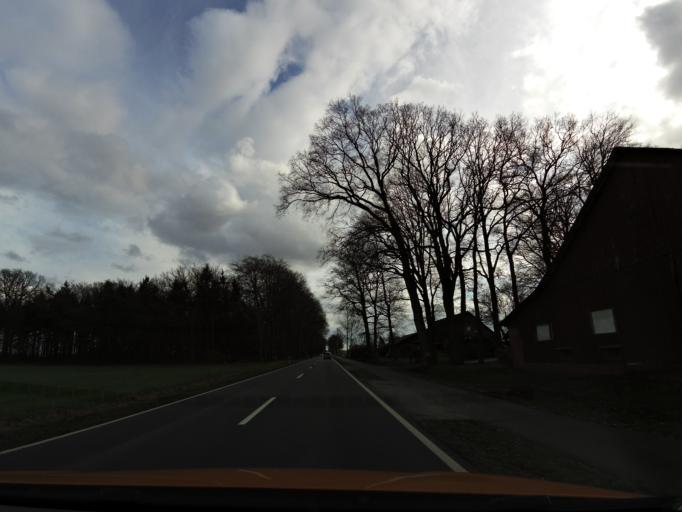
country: DE
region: Lower Saxony
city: Dotlingen
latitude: 52.9608
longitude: 8.4044
